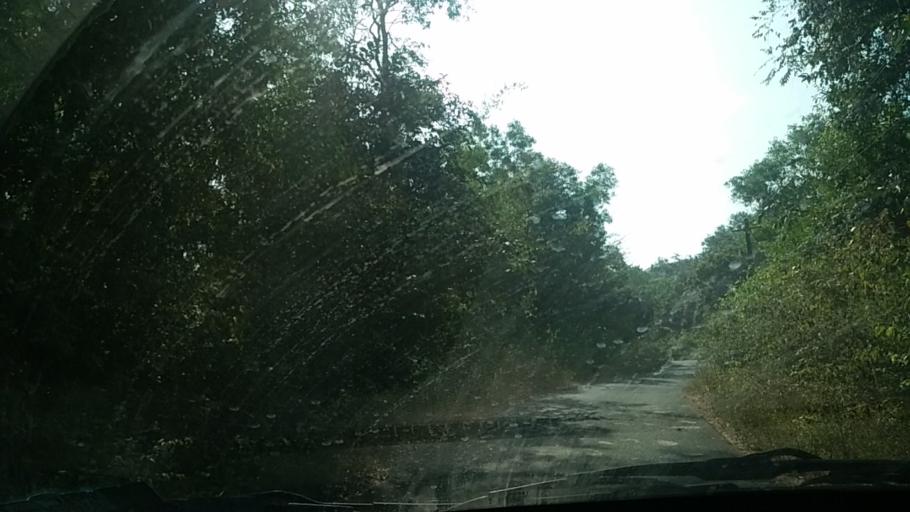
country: IN
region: Goa
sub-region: North Goa
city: Ponda
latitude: 15.3703
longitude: 74.0868
